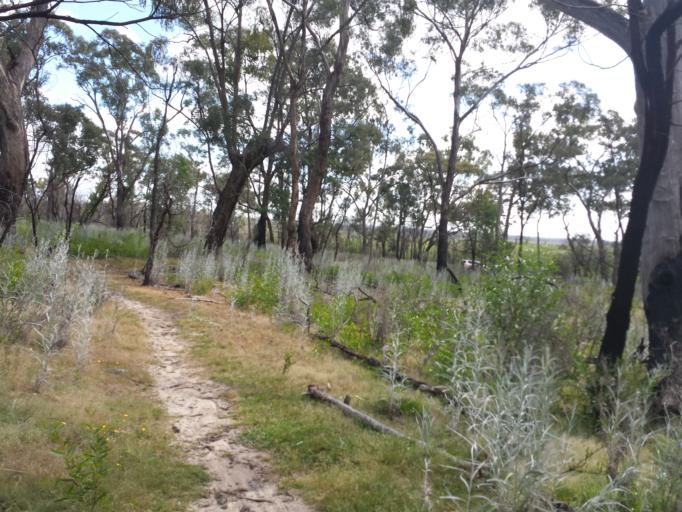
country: AU
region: Victoria
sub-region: Southern Grampians
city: Hamilton
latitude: -37.2687
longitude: 142.2704
